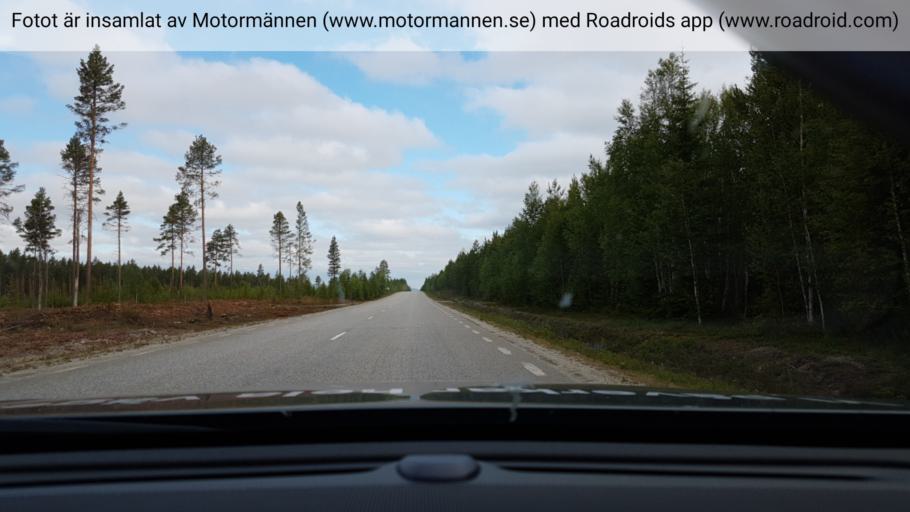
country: SE
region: Vaesterbotten
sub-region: Norsjo Kommun
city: Norsjoe
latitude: 64.5480
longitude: 19.3302
